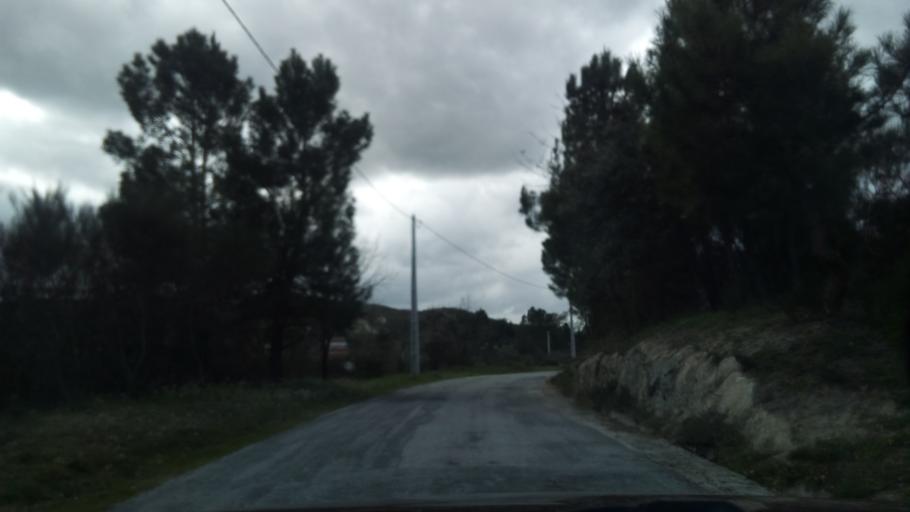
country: PT
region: Guarda
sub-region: Fornos de Algodres
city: Fornos de Algodres
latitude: 40.5847
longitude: -7.5560
